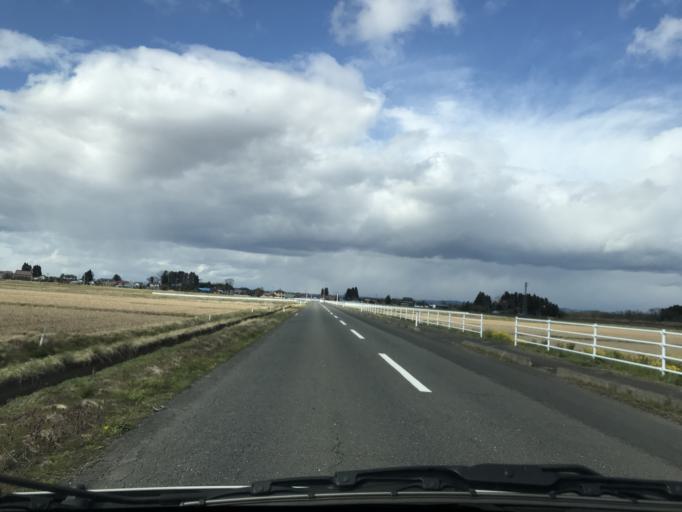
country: JP
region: Miyagi
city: Wakuya
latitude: 38.6515
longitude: 141.2037
